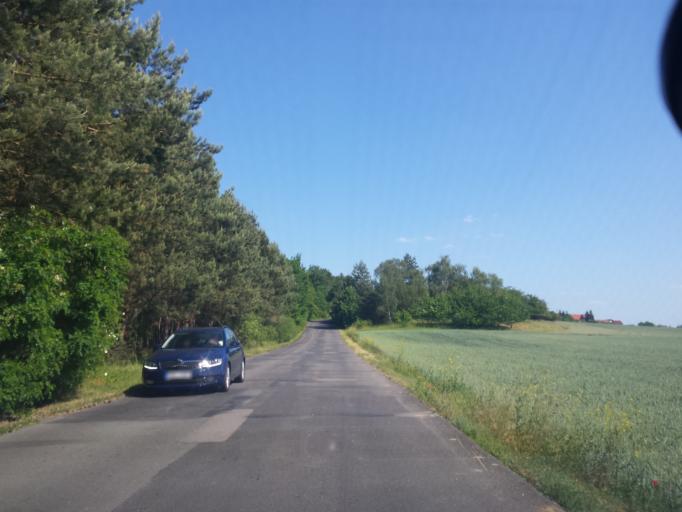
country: CZ
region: Central Bohemia
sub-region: Okres Melnik
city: Melnik
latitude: 50.3796
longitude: 14.4910
